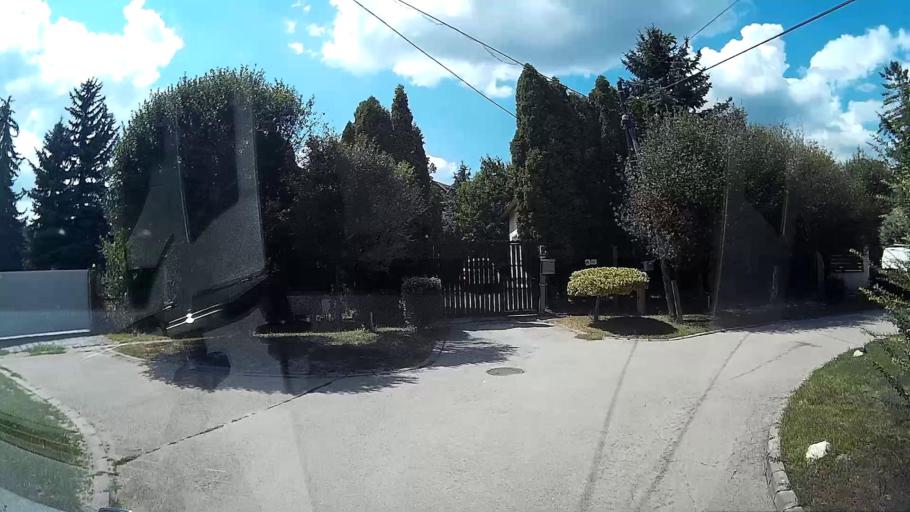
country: HU
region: Pest
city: Szentendre
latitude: 47.6700
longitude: 19.0611
